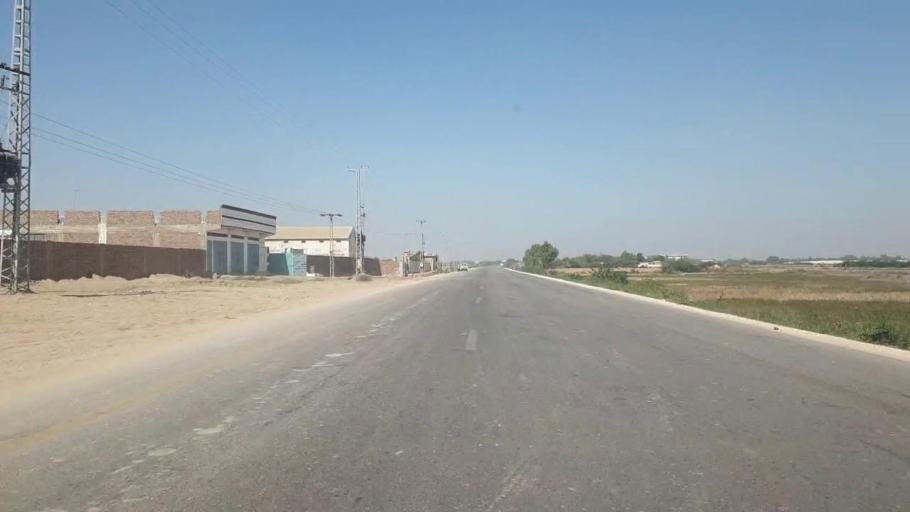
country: PK
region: Sindh
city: Talhar
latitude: 24.8671
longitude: 68.8167
